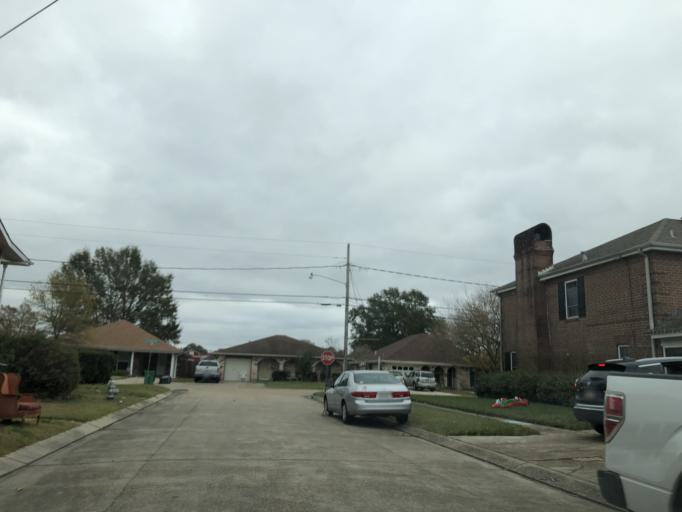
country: US
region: Louisiana
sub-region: Jefferson Parish
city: Metairie Terrace
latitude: 29.9904
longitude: -90.1631
